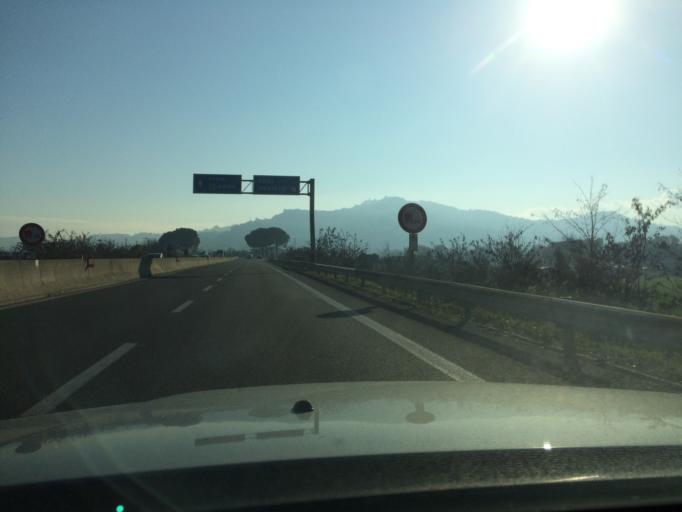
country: IT
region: Umbria
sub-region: Provincia di Perugia
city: Ponterio-Pian di Porto
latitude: 42.8069
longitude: 12.4069
